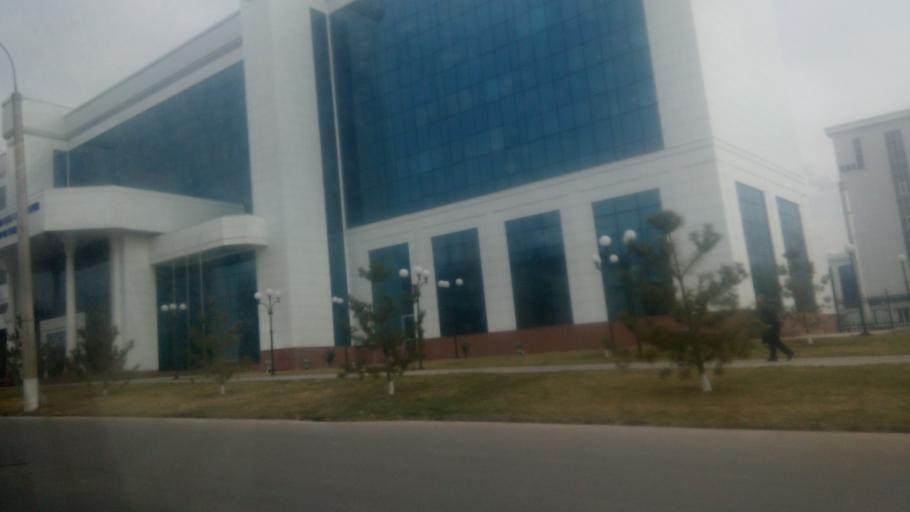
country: UZ
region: Toshkent
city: Salor
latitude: 41.3382
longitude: 69.3332
